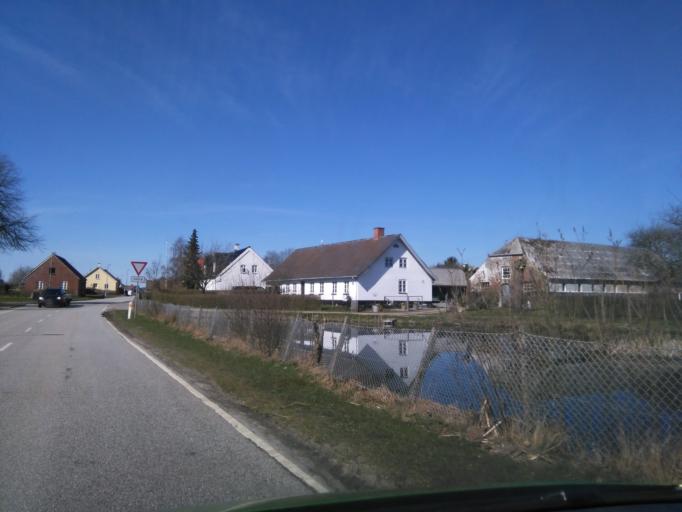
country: DK
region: Central Jutland
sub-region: Horsens Kommune
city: Braedstrup
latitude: 56.0202
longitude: 9.6465
